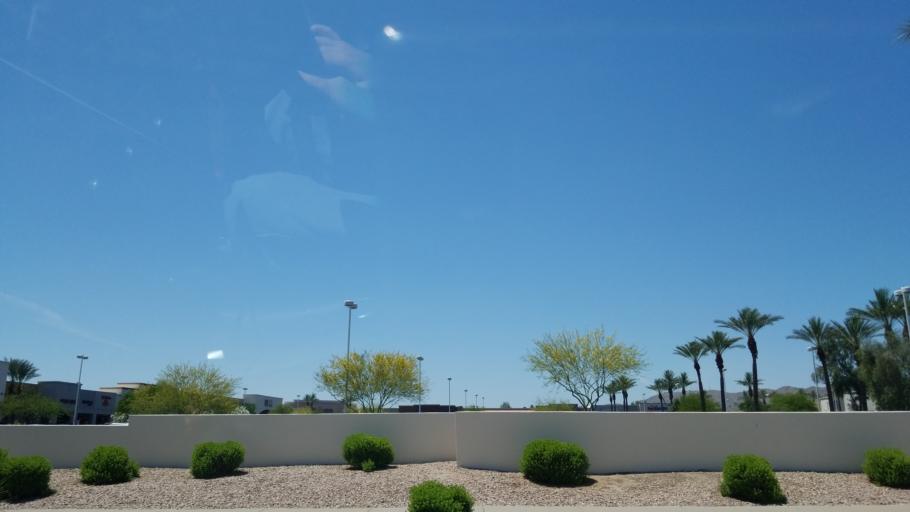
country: US
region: Arizona
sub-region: Maricopa County
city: Guadalupe
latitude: 33.3186
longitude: -111.9806
